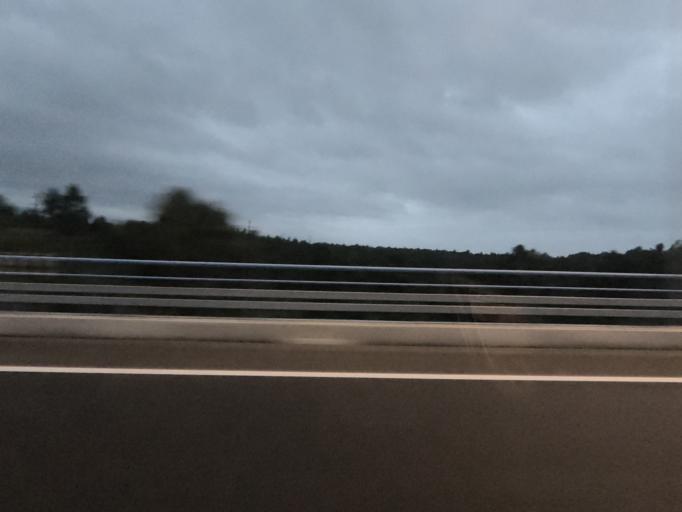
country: PT
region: Setubal
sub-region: Seixal
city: Arrentela
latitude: 38.6024
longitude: -9.1144
